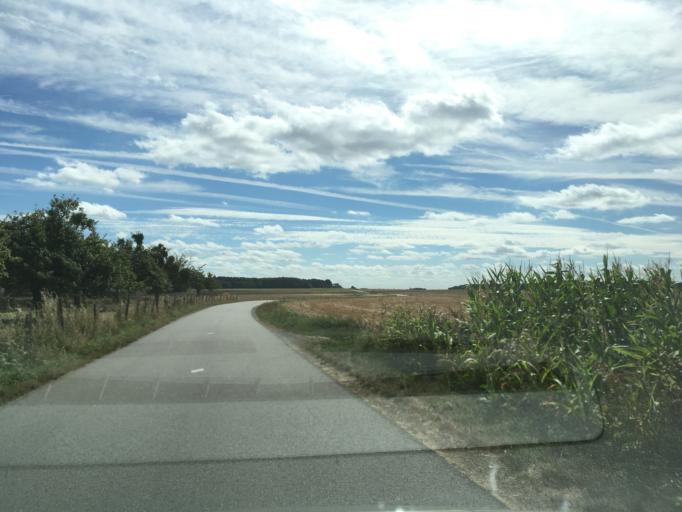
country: FR
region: Haute-Normandie
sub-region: Departement de l'Eure
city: Heudreville-sur-Eure
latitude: 49.1574
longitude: 1.2575
